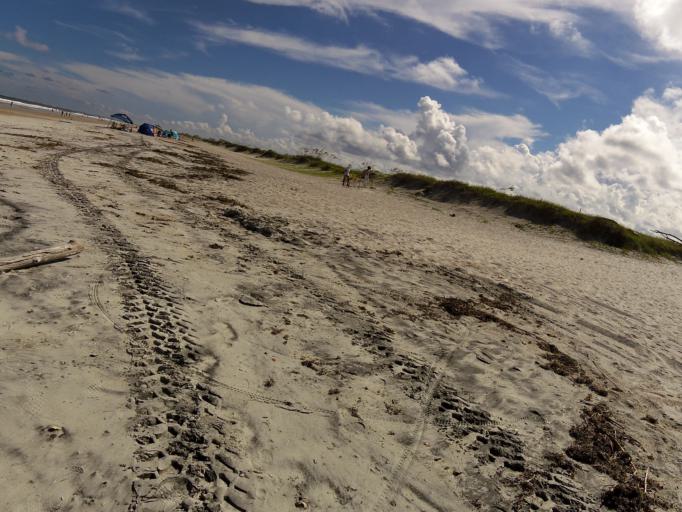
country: US
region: Florida
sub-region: Duval County
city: Atlantic Beach
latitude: 30.4595
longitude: -81.4112
